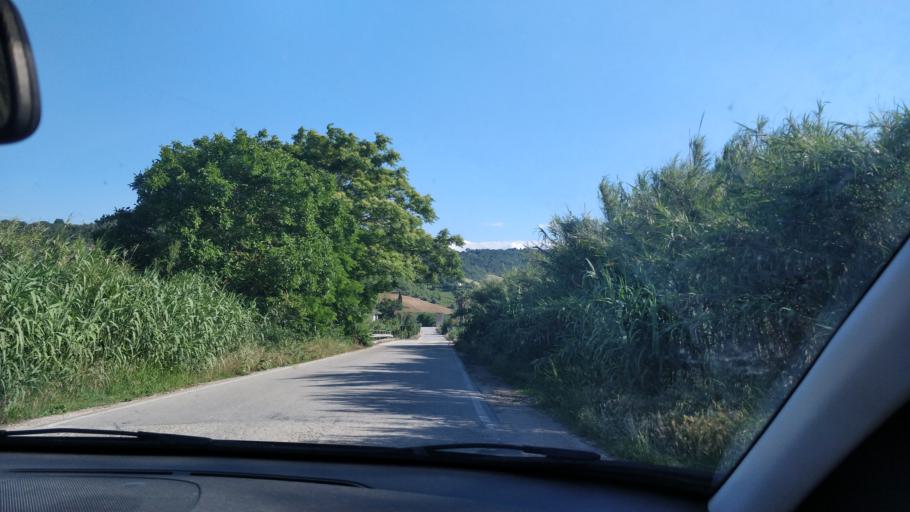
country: IT
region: The Marches
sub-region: Provincia di Ascoli Piceno
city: Massignano
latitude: 43.0372
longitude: 13.8002
